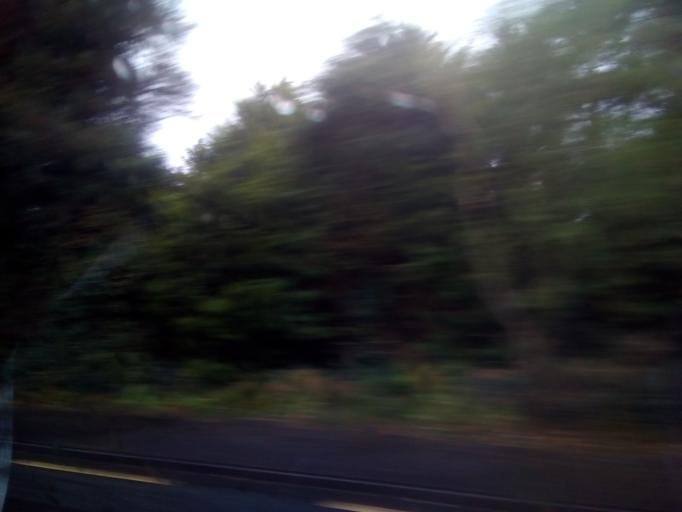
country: IE
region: Connaught
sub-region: Roscommon
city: Castlerea
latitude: 53.8388
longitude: -8.3838
